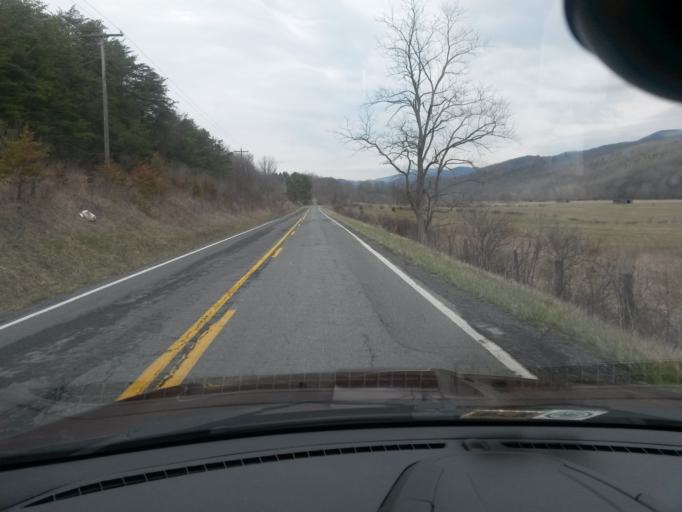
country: US
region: Virginia
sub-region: Highland County
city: Monterey
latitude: 38.2696
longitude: -79.6717
